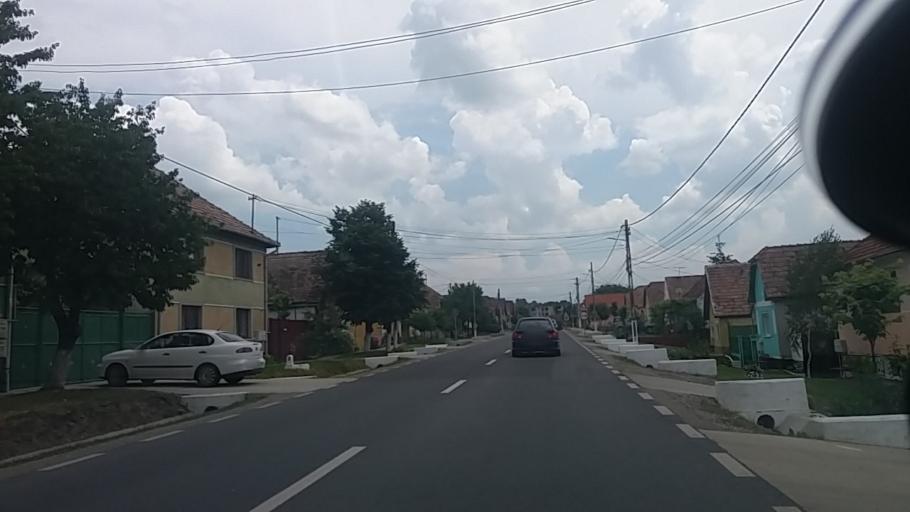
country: RO
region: Sibiu
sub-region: Comuna Slimnic
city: Slimnic
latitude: 45.9654
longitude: 24.1604
